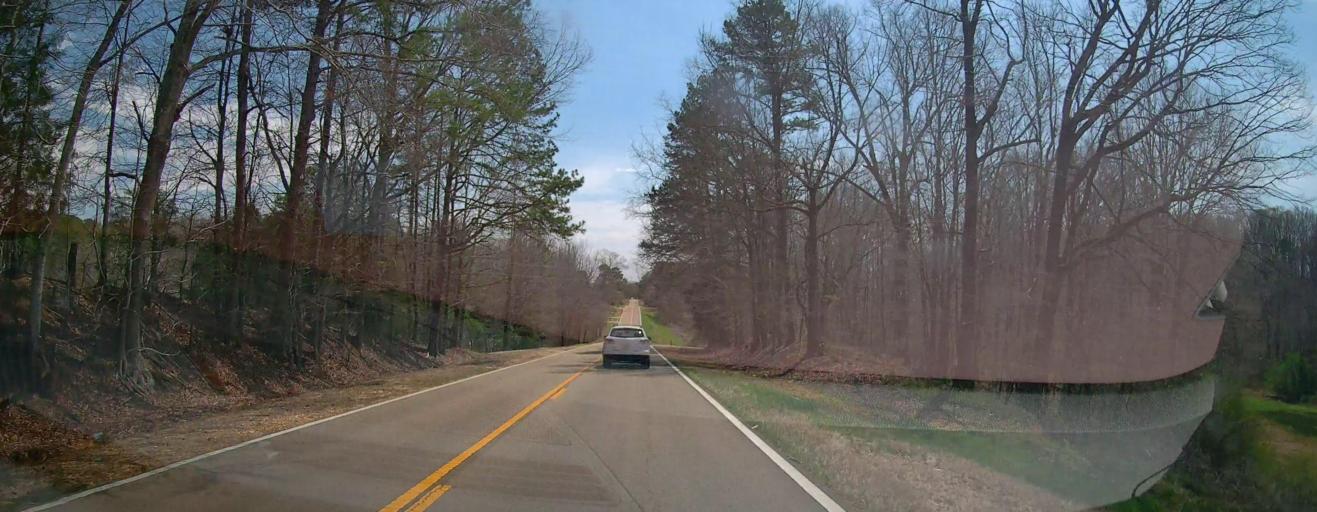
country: US
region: Mississippi
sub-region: Union County
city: New Albany
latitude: 34.4332
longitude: -88.9537
